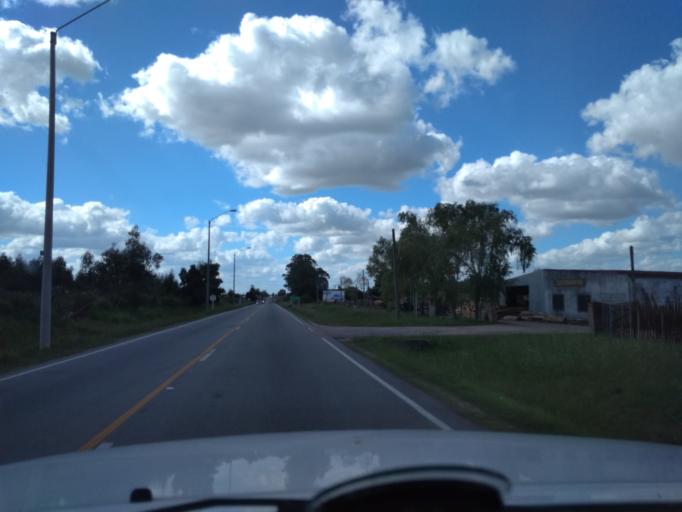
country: UY
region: Canelones
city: Joaquin Suarez
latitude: -34.7109
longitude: -56.0594
